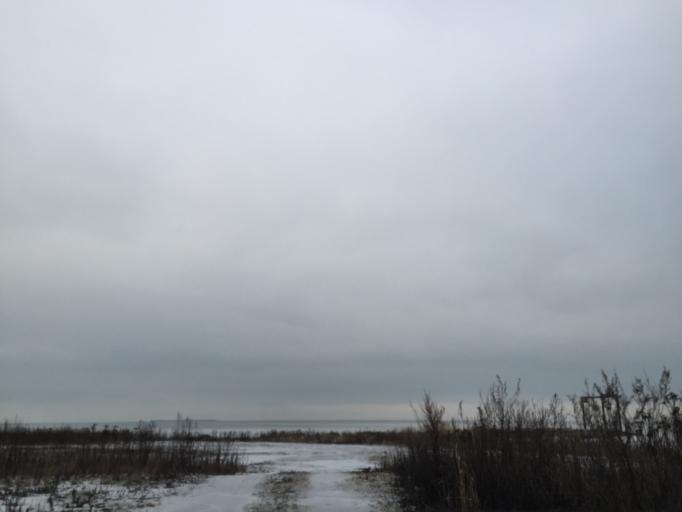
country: EE
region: Saare
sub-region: Orissaare vald
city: Orissaare
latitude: 58.6829
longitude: 23.1939
